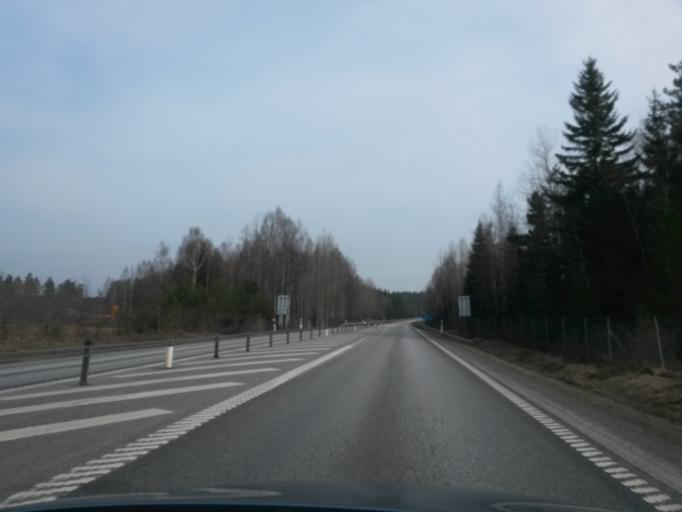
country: SE
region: Vaestra Goetaland
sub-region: Gullspangs Kommun
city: Anderstorp
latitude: 58.9385
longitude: 14.4336
